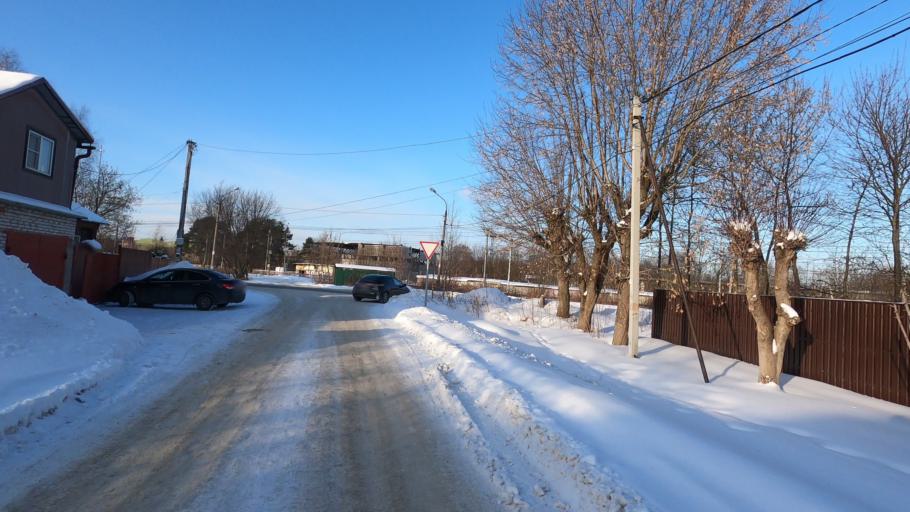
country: RU
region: Moskovskaya
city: Pavlovskiy Posad
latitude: 55.7722
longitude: 38.6975
